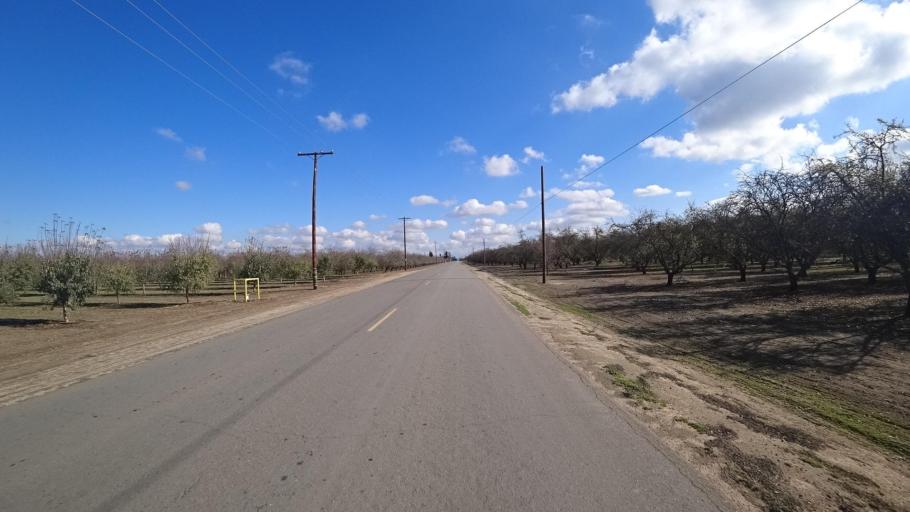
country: US
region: California
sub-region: Kern County
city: McFarland
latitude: 35.6887
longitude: -119.2904
